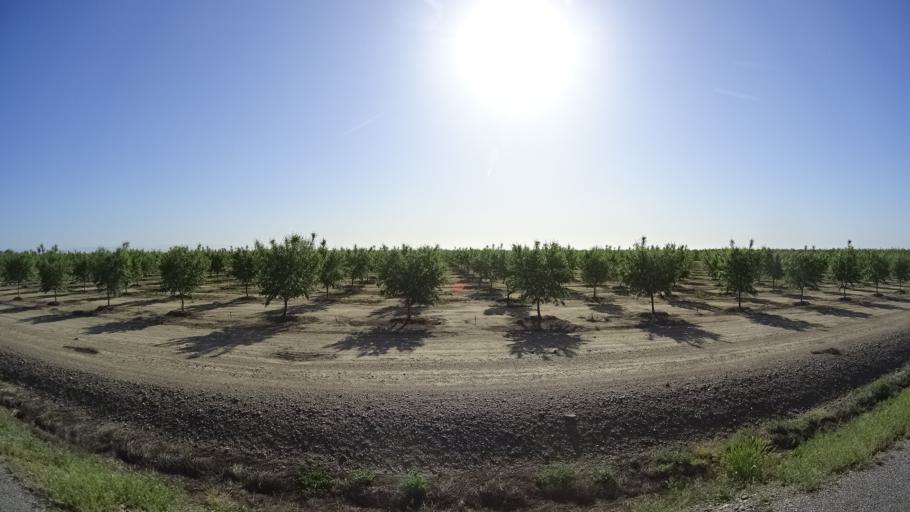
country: US
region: California
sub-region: Glenn County
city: Orland
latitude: 39.6864
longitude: -122.1220
